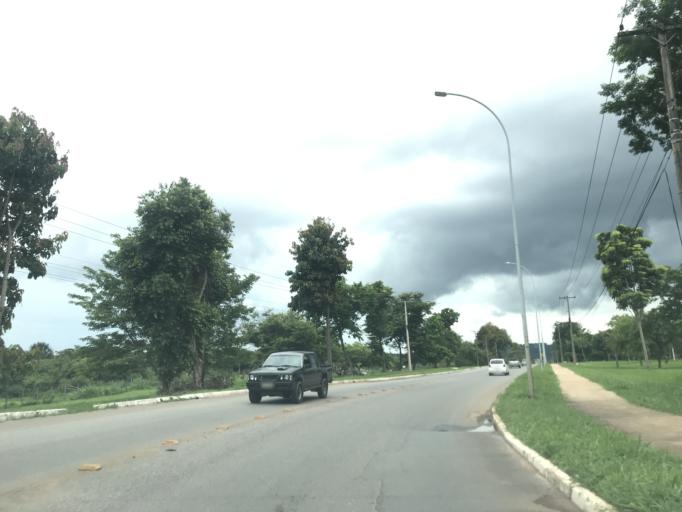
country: BR
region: Federal District
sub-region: Brasilia
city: Brasilia
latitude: -15.6542
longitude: -47.8140
